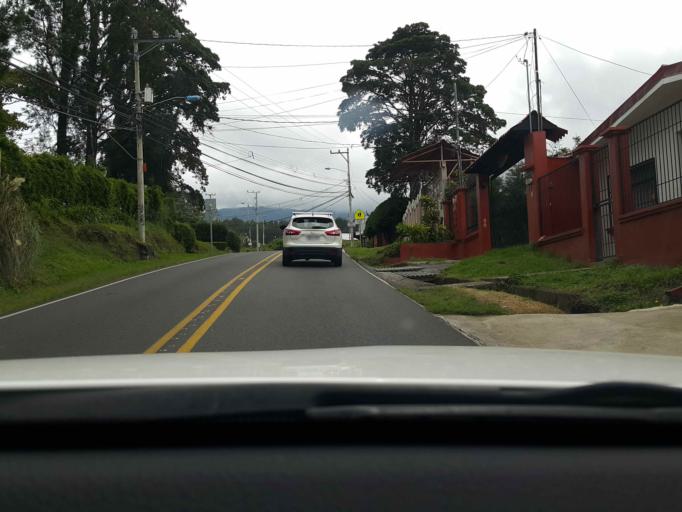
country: CR
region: Heredia
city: San Josecito
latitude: 10.0356
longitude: -84.0901
